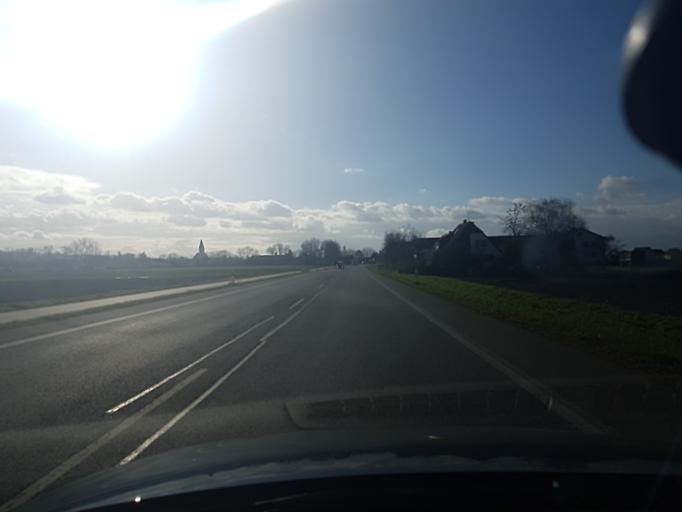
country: DE
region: Bavaria
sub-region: Lower Bavaria
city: Niederaichbach
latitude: 48.6088
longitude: 12.2843
